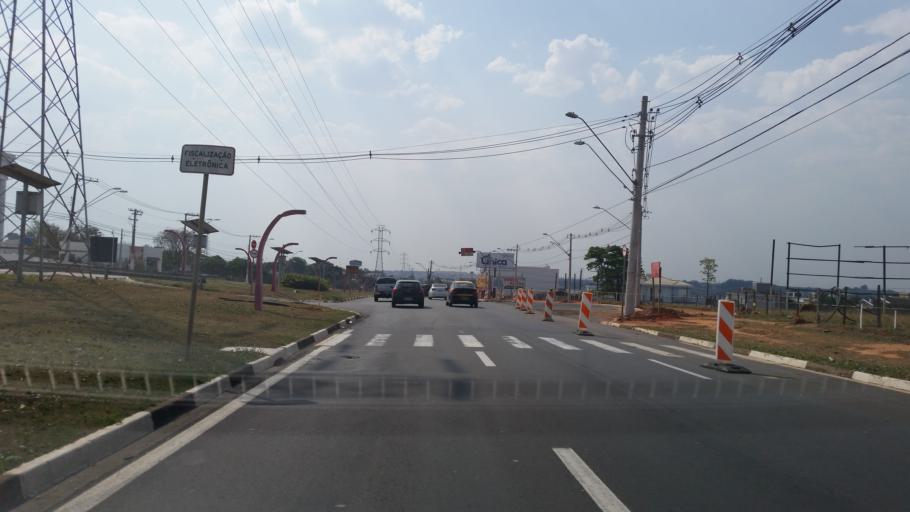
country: BR
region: Sao Paulo
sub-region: Hortolandia
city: Hortolandia
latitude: -22.8871
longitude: -47.1930
